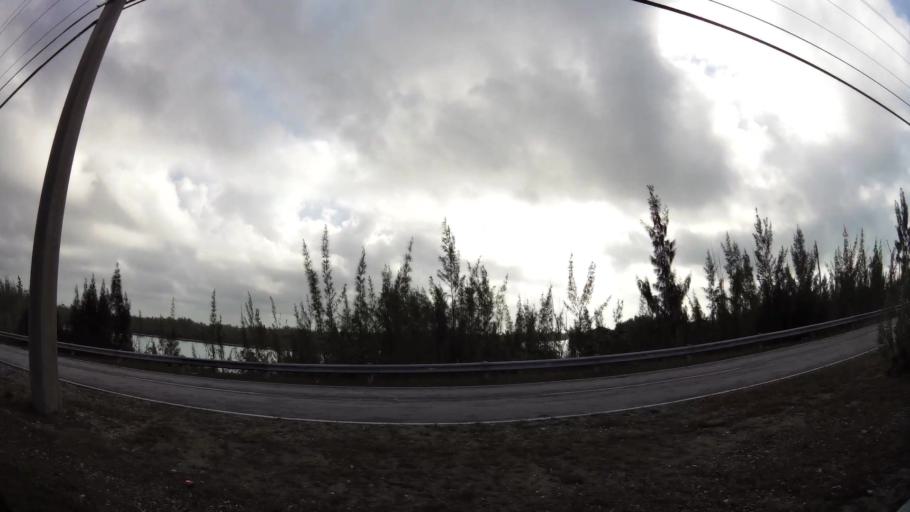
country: BS
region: Freeport
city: Lucaya
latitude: 26.5739
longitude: -78.5815
